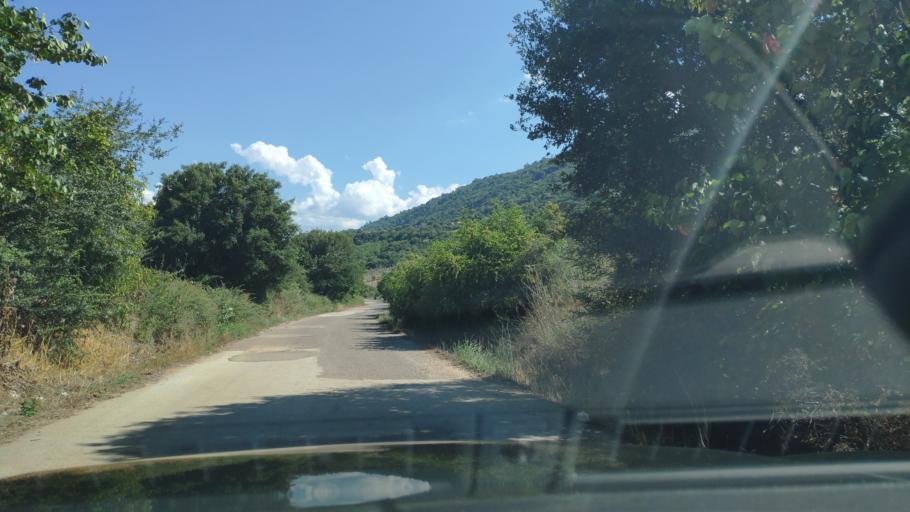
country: GR
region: West Greece
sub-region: Nomos Aitolias kai Akarnanias
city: Katouna
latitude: 38.8421
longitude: 21.0955
